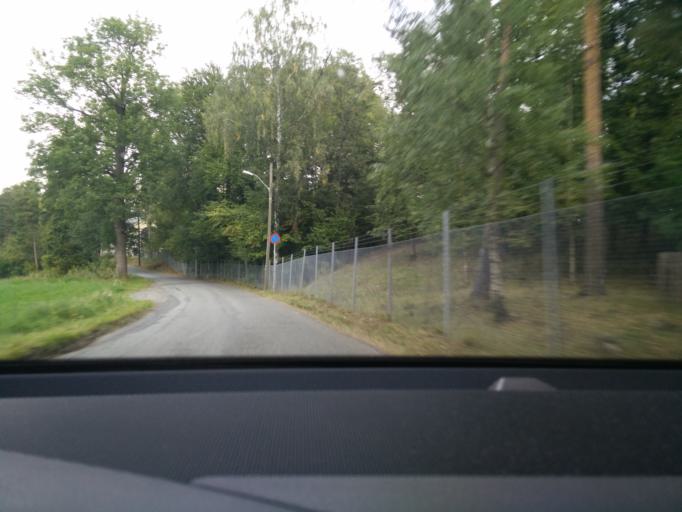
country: NO
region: Oslo
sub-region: Oslo
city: Sjolyststranda
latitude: 59.9069
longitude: 10.6811
